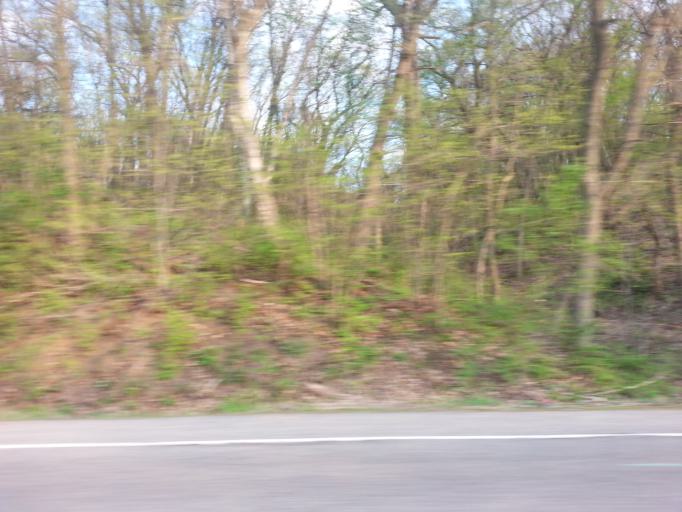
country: US
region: Minnesota
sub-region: Dakota County
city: Mendota Heights
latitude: 44.8893
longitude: -93.1557
